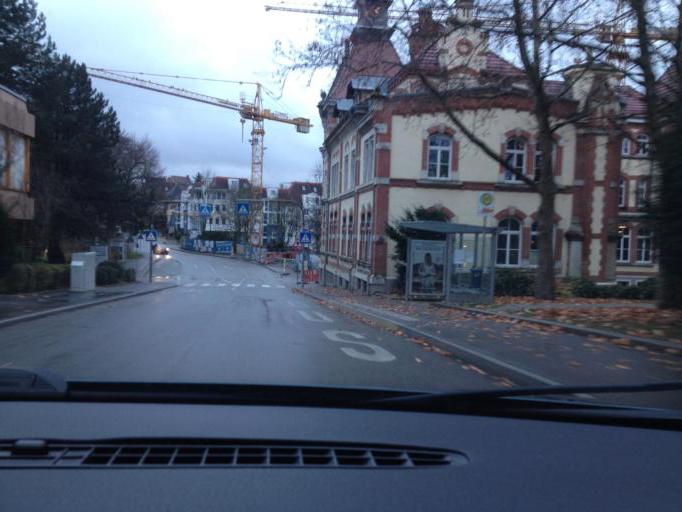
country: DE
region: Baden-Wuerttemberg
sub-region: Regierungsbezirk Stuttgart
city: Ludwigsburg
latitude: 48.8983
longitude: 9.2047
